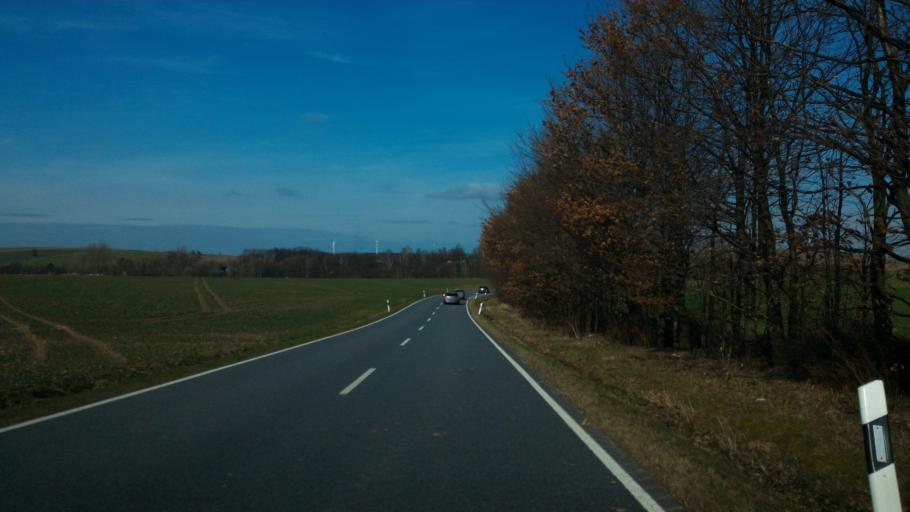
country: DE
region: Saxony
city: Stolpen
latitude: 51.0318
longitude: 14.1310
